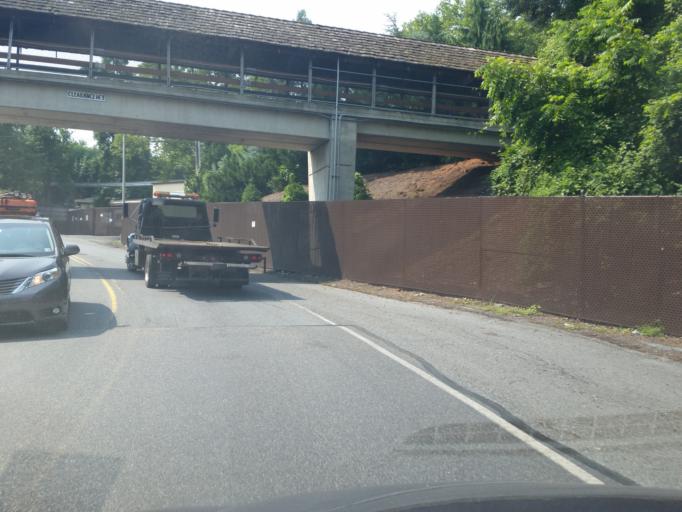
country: US
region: Pennsylvania
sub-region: Dauphin County
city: Hershey
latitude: 40.2883
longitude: -76.6527
